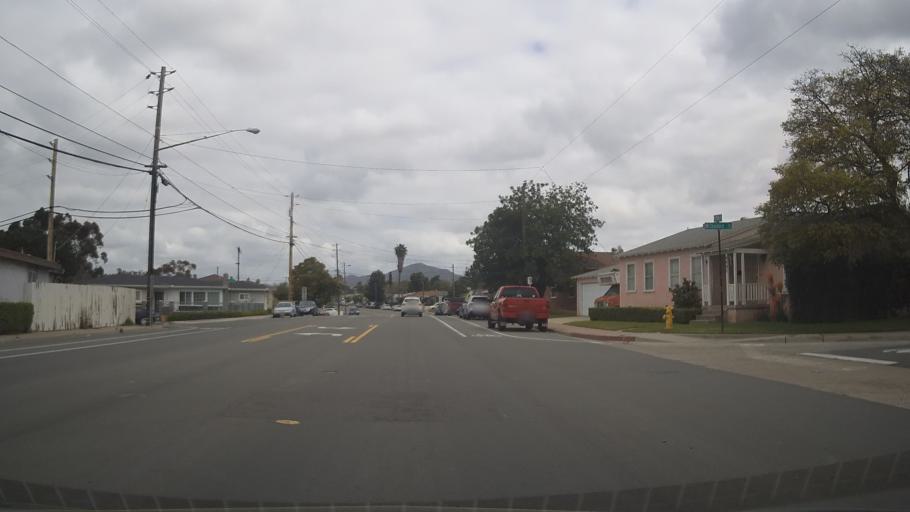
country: US
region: California
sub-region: San Diego County
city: Lemon Grove
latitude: 32.7593
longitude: -117.0473
